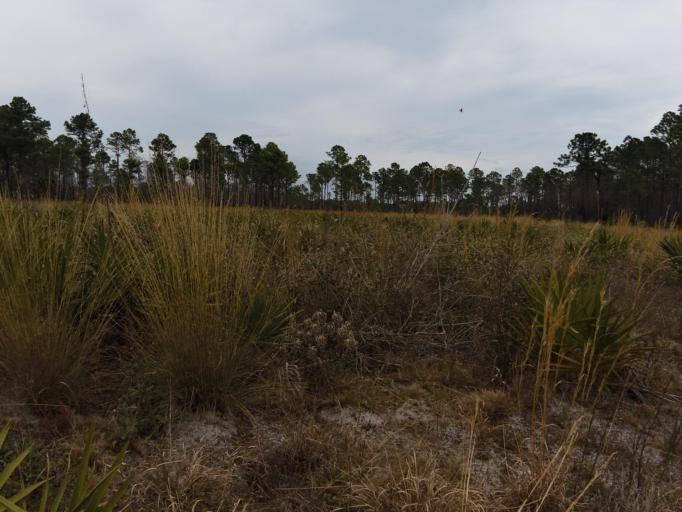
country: US
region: Florida
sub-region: Duval County
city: Atlantic Beach
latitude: 30.4709
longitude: -81.5043
